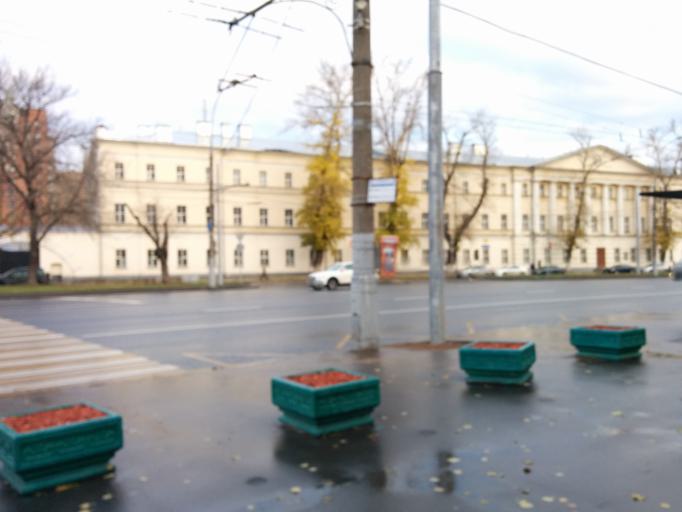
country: RU
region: Moskovskaya
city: Dorogomilovo
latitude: 55.7284
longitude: 37.5842
